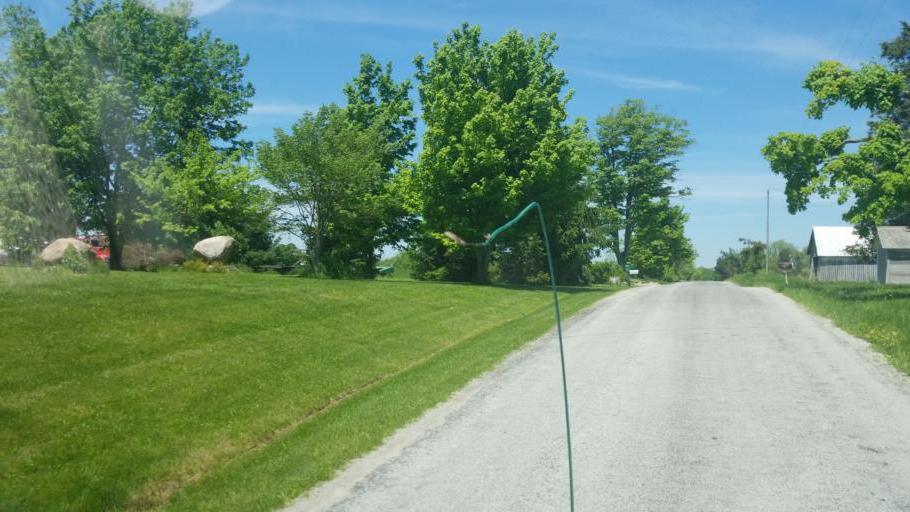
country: US
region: Ohio
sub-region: Huron County
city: Greenwich
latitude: 41.0001
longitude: -82.4332
